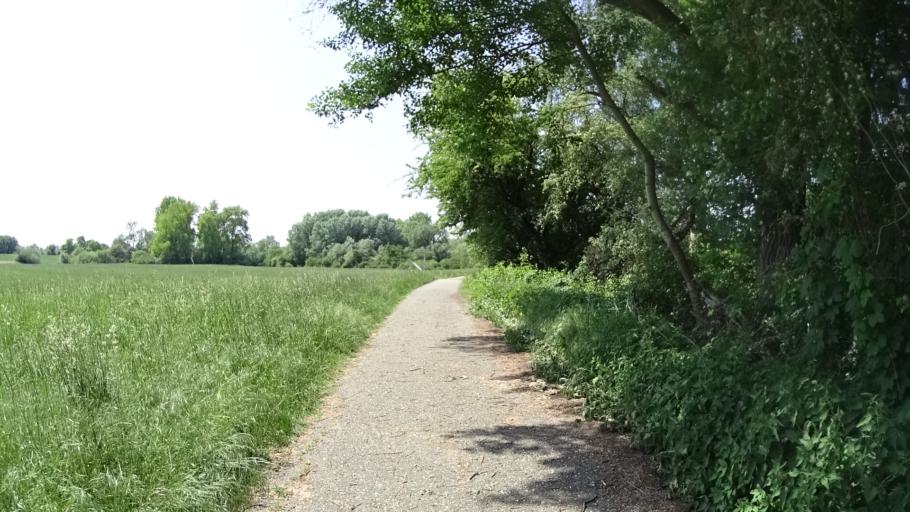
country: DE
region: Baden-Wuerttemberg
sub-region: Karlsruhe Region
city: Bruhl
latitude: 49.4166
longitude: 8.5147
